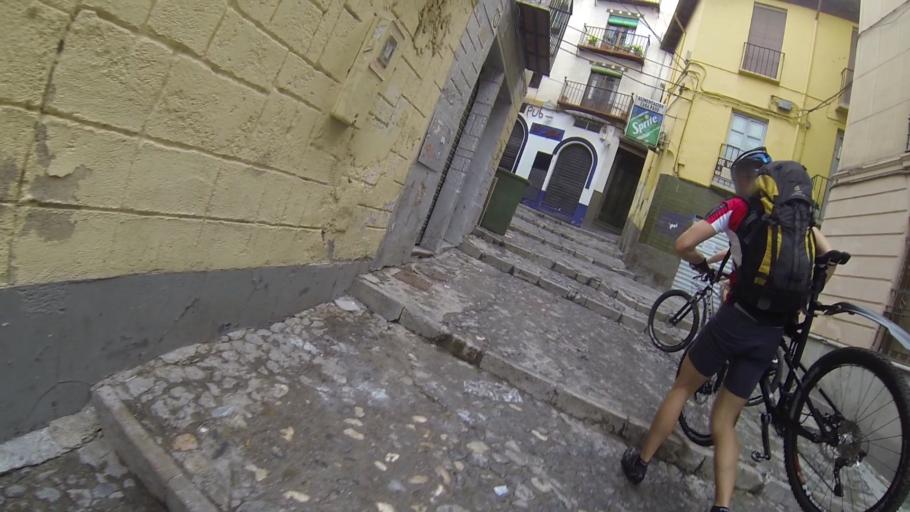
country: ES
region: Andalusia
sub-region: Provincia de Granada
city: Granada
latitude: 37.1763
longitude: -3.5960
